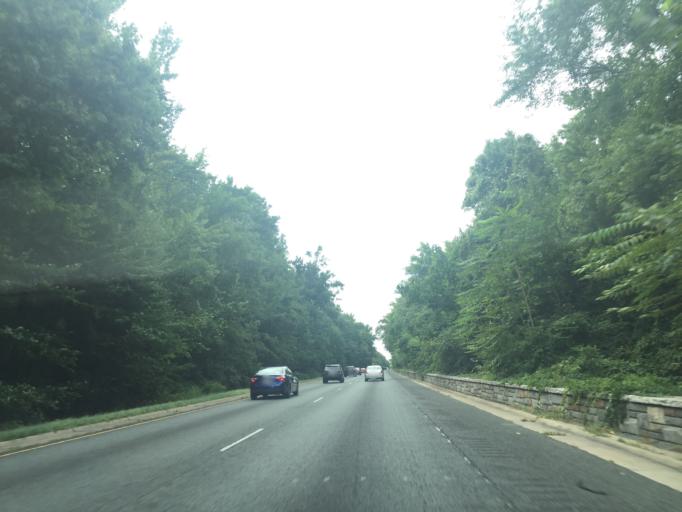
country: US
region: Maryland
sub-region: Anne Arundel County
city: Jessup
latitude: 39.1277
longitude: -76.7635
